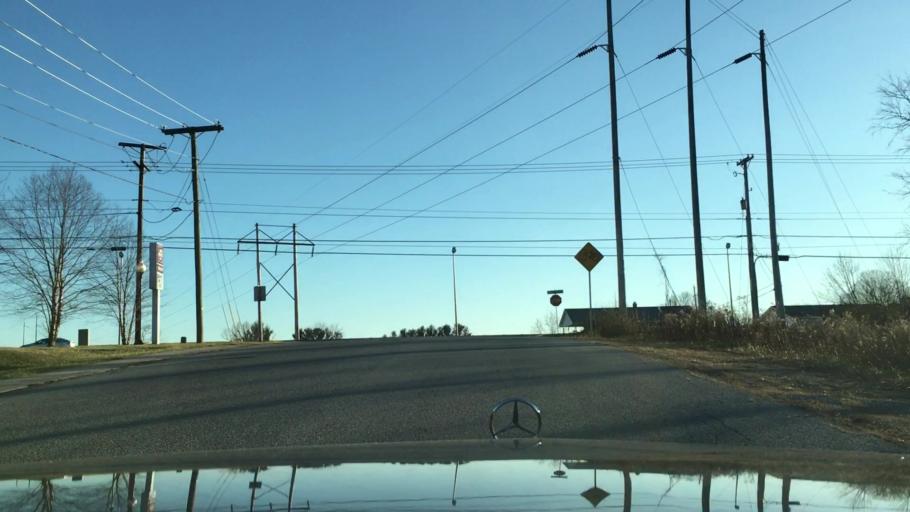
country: US
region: Virginia
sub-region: Montgomery County
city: Merrimac
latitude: 37.1635
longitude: -80.4436
